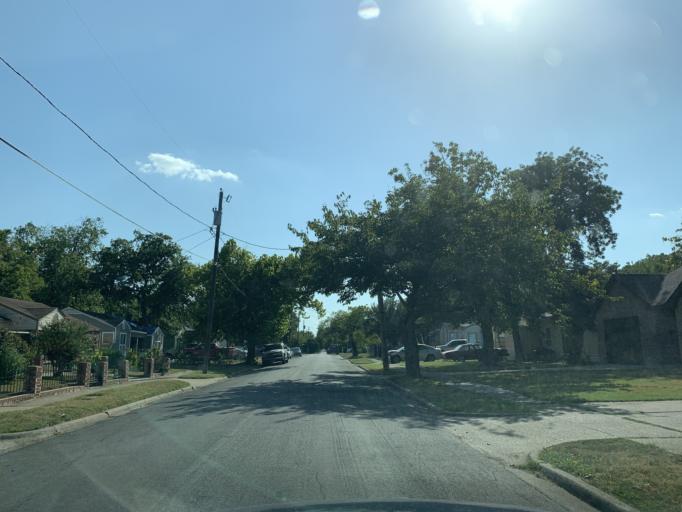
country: US
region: Texas
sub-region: Dallas County
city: Dallas
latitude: 32.7047
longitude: -96.7899
